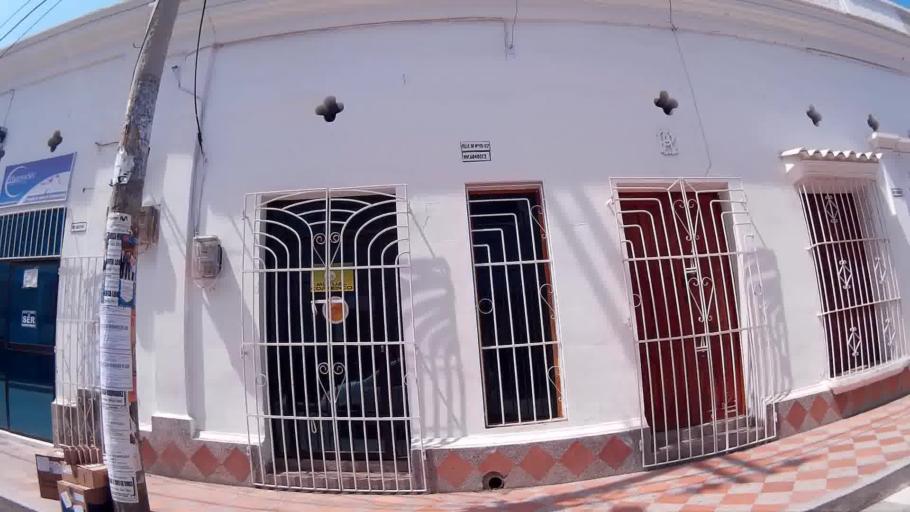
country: CO
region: Magdalena
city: Cienaga
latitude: 11.0105
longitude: -74.2499
